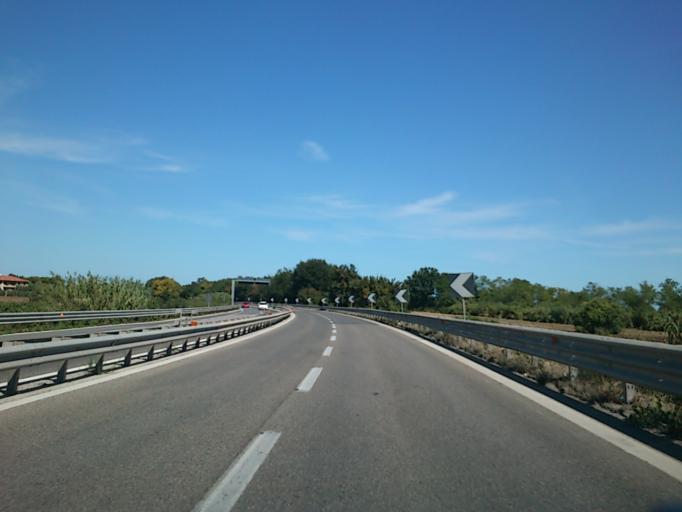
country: IT
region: The Marches
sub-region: Provincia di Pesaro e Urbino
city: Bellocchi
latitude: 43.8064
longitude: 13.0172
